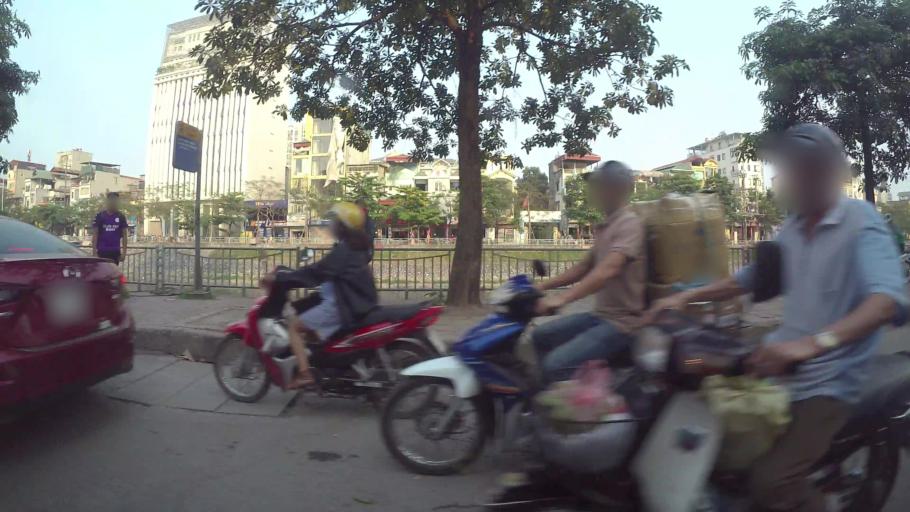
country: VN
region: Ha Noi
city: Thanh Xuan
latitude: 20.9948
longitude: 105.8144
